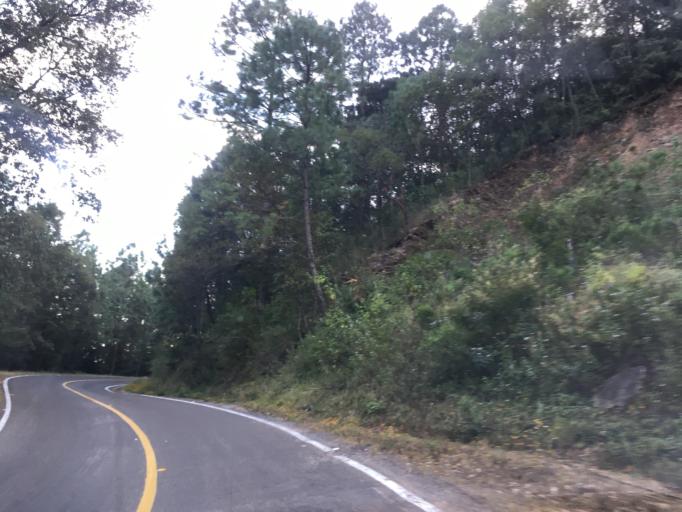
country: MX
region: Michoacan
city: Tzitzio
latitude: 19.6701
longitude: -100.9235
